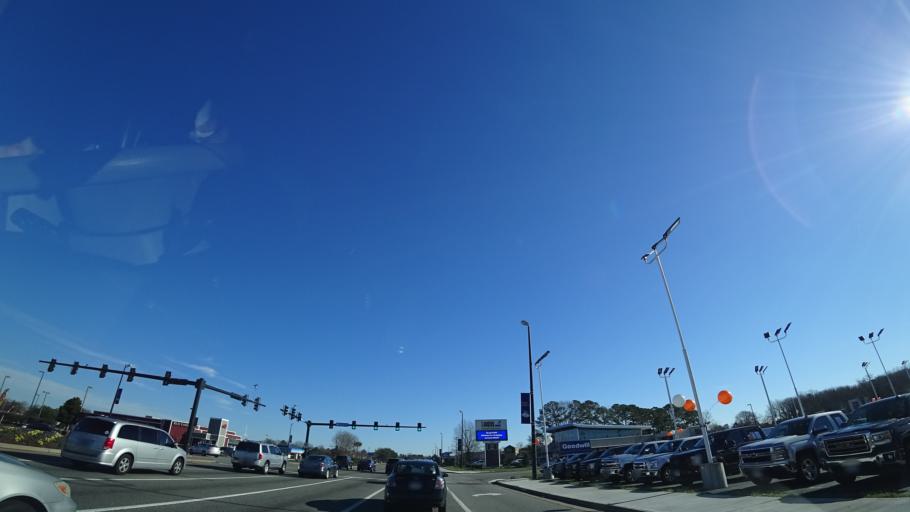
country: US
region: Virginia
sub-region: City of Hampton
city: Hampton
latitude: 37.0420
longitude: -76.3845
